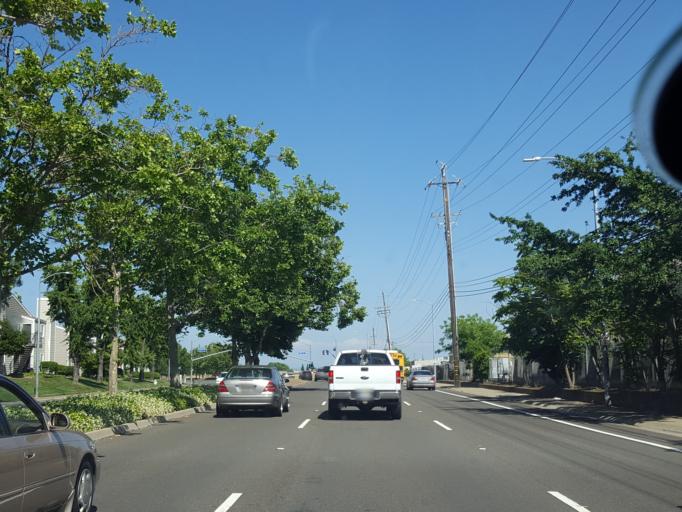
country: US
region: California
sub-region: Sacramento County
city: Rancho Cordova
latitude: 38.5739
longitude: -121.2977
